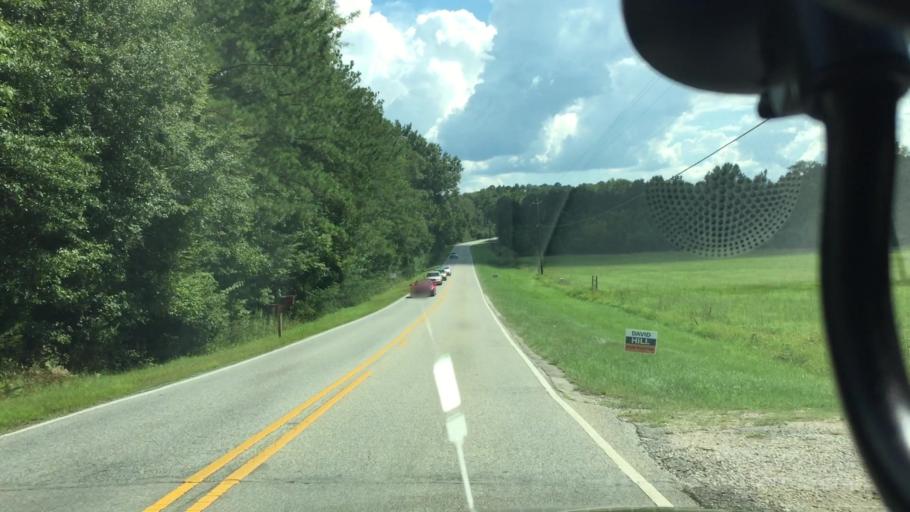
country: US
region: Alabama
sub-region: Lee County
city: Auburn
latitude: 32.5666
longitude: -85.5243
